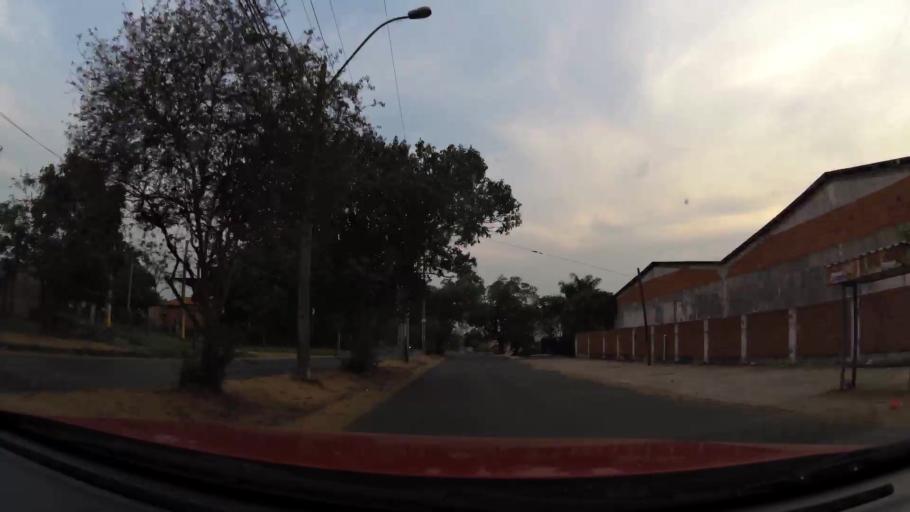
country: PY
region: Central
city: Lambare
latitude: -25.3492
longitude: -57.6405
